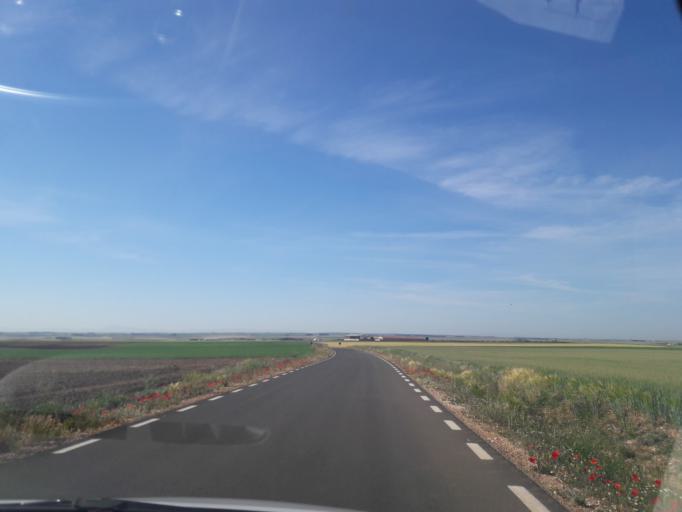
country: ES
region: Castille and Leon
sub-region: Provincia de Salamanca
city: Parada de Rubiales
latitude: 41.1349
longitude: -5.4305
